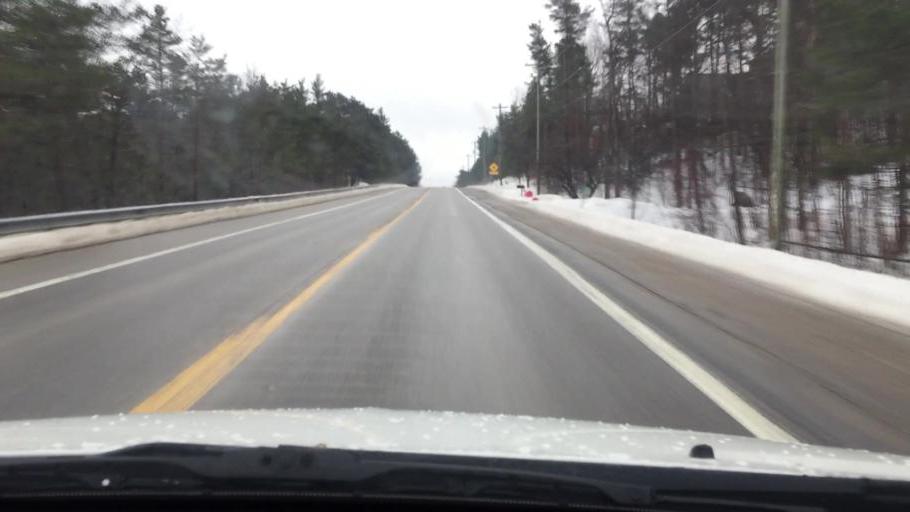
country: US
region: Michigan
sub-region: Charlevoix County
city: Charlevoix
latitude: 45.2676
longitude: -85.2055
